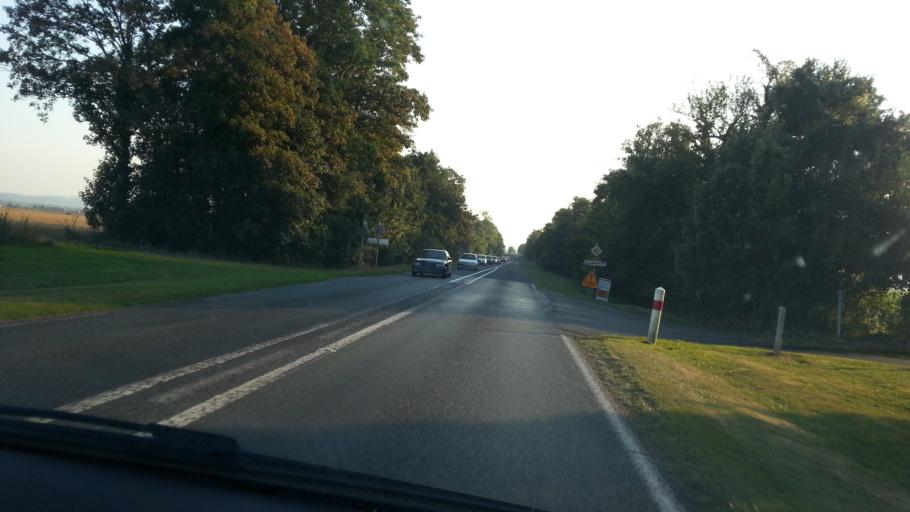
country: FR
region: Picardie
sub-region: Departement de l'Oise
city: Grandfresnoy
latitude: 49.3798
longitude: 2.6187
